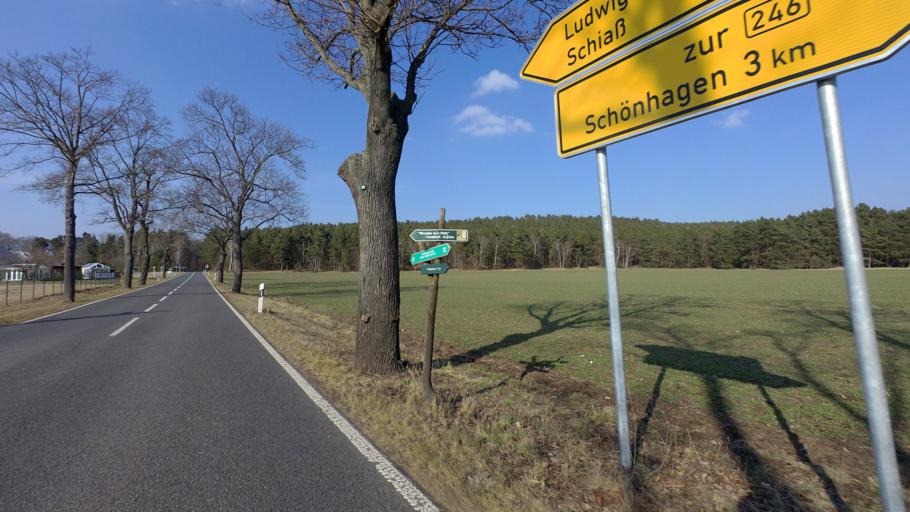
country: DE
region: Brandenburg
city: Trebbin
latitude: 52.2414
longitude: 13.1346
